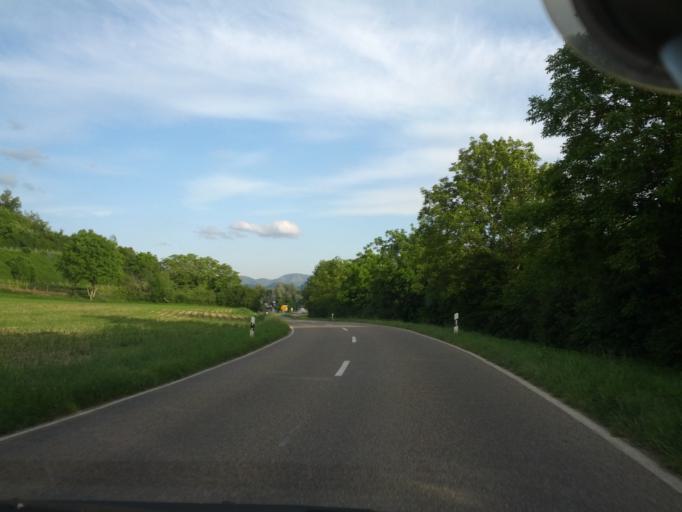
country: DE
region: Baden-Wuerttemberg
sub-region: Freiburg Region
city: Unterkrozingen
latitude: 47.9668
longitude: 7.6839
